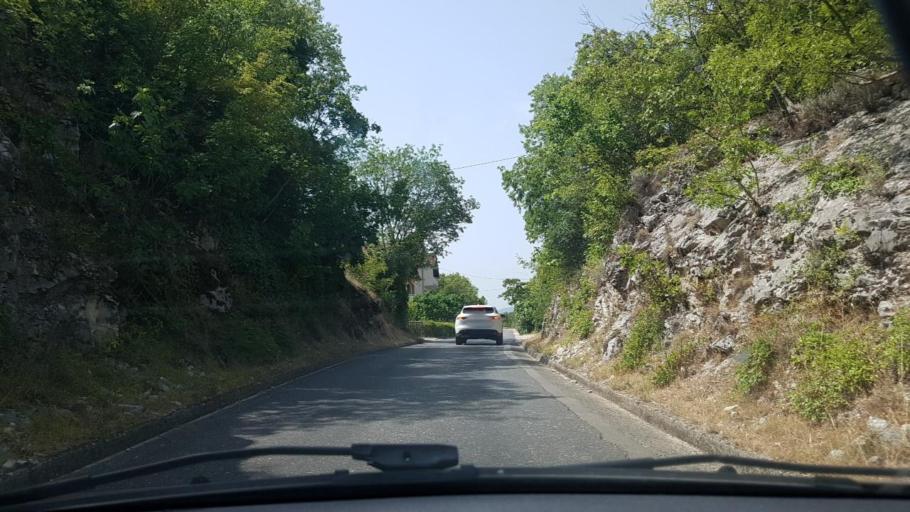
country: BA
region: Federation of Bosnia and Herzegovina
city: Tasovcici
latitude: 43.0346
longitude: 17.7260
